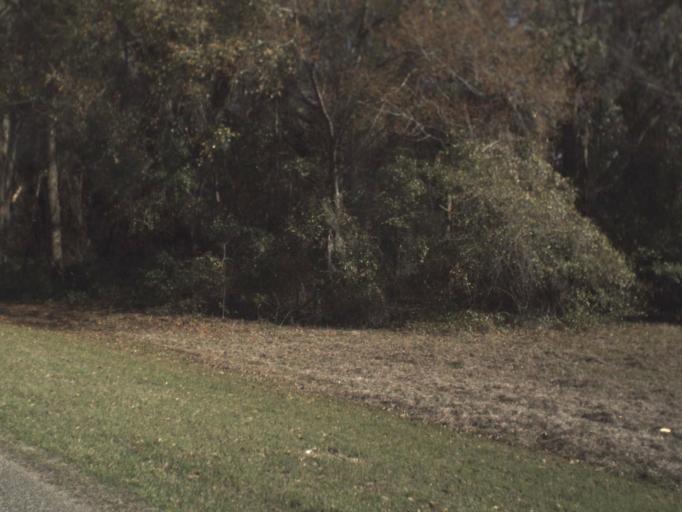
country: US
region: Florida
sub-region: Jackson County
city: Malone
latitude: 30.9691
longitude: -85.1630
